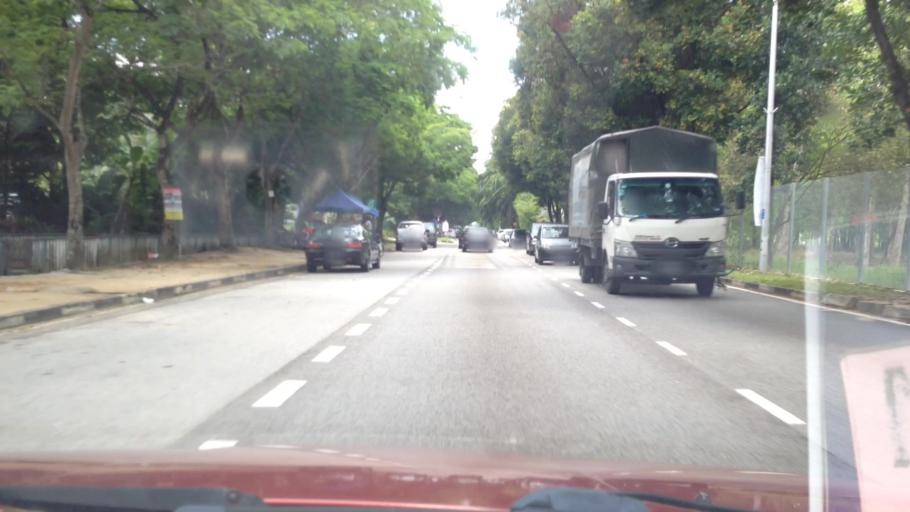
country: MY
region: Selangor
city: Kampung Baru Subang
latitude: 3.1704
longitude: 101.5505
